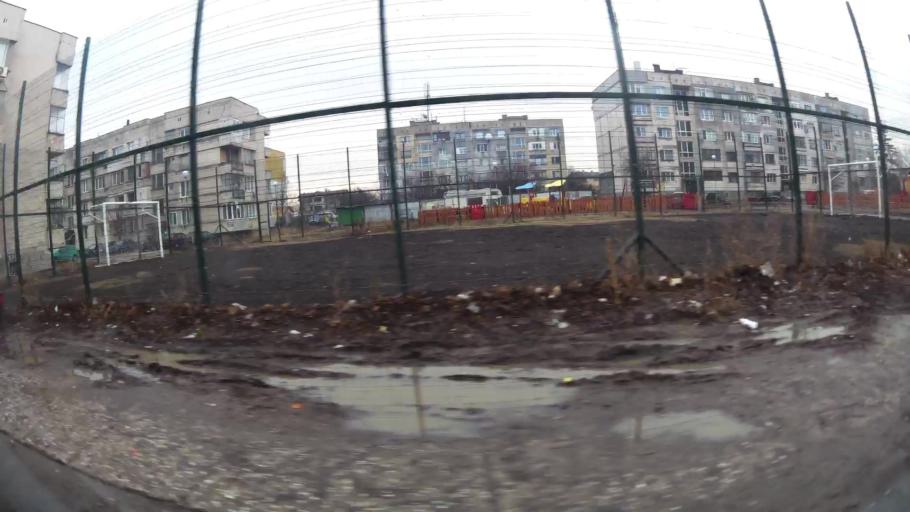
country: BG
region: Sofia-Capital
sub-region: Stolichna Obshtina
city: Sofia
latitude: 42.7408
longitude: 23.3431
